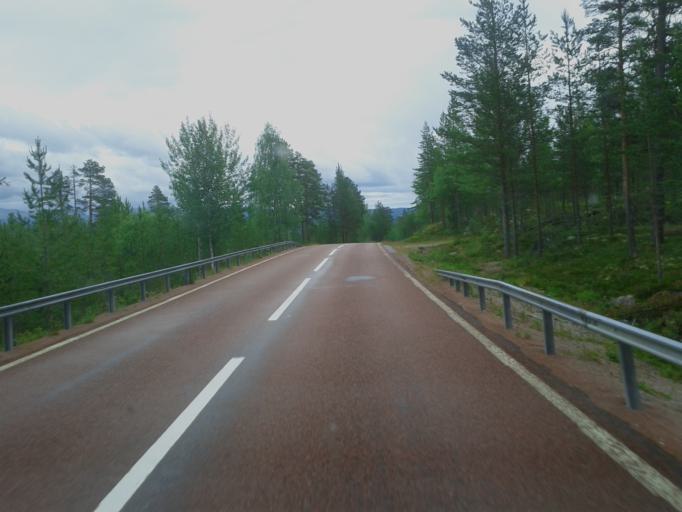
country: NO
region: Hedmark
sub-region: Trysil
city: Innbygda
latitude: 61.8527
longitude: 12.6288
